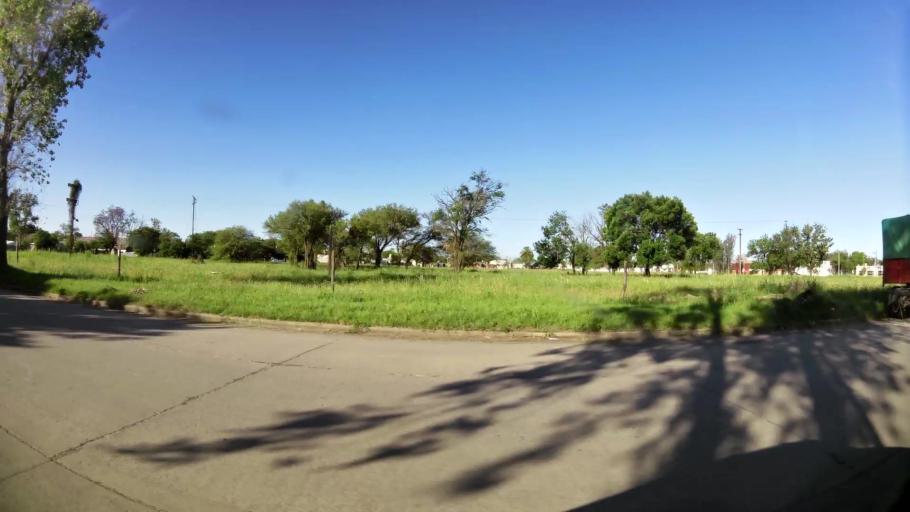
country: AR
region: Cordoba
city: San Francisco
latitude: -31.4341
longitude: -62.0685
